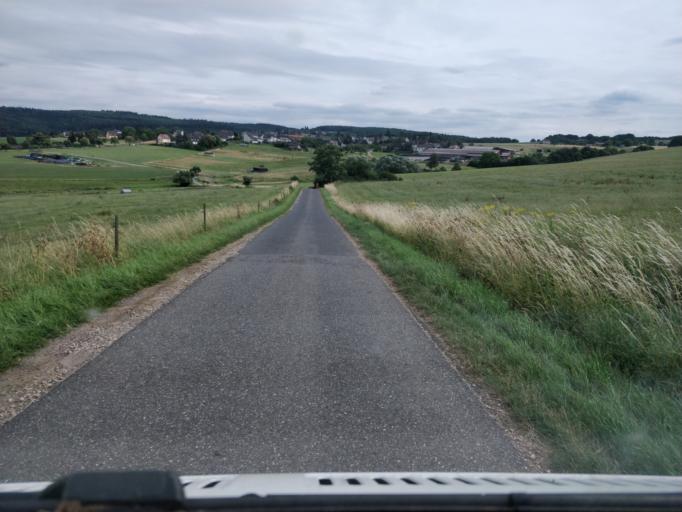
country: DE
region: North Rhine-Westphalia
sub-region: Regierungsbezirk Koln
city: Rheinbach
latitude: 50.5988
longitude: 6.9264
